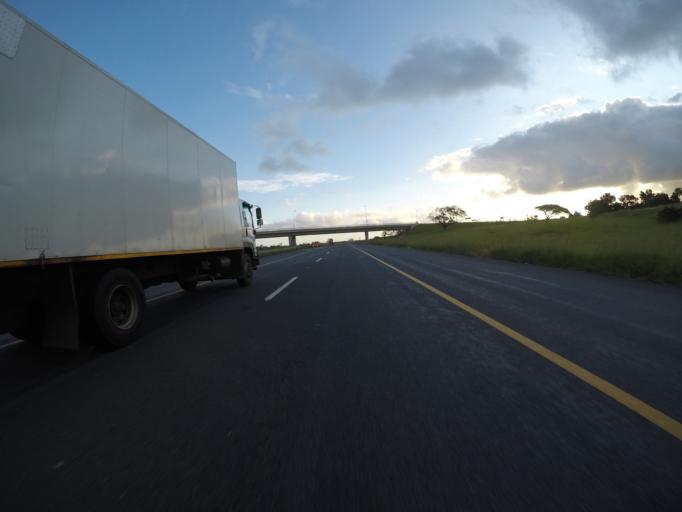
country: ZA
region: KwaZulu-Natal
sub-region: uThungulu District Municipality
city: KwaMbonambi
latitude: -28.5982
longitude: 32.0976
